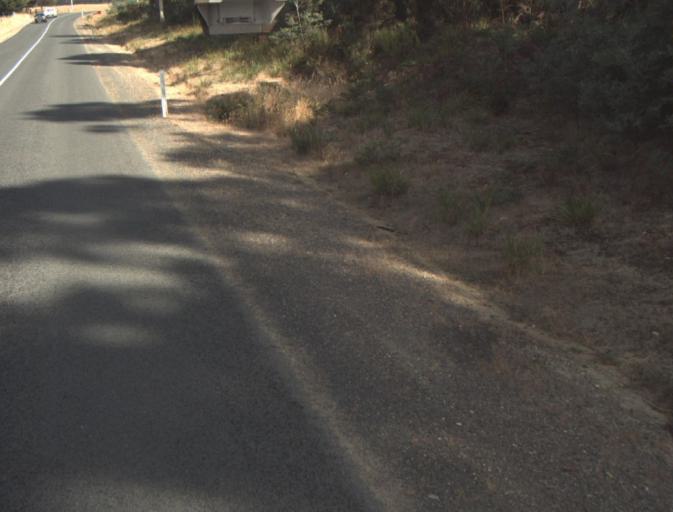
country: AU
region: Tasmania
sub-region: Dorset
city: Bridport
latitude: -41.1335
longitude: 147.2196
